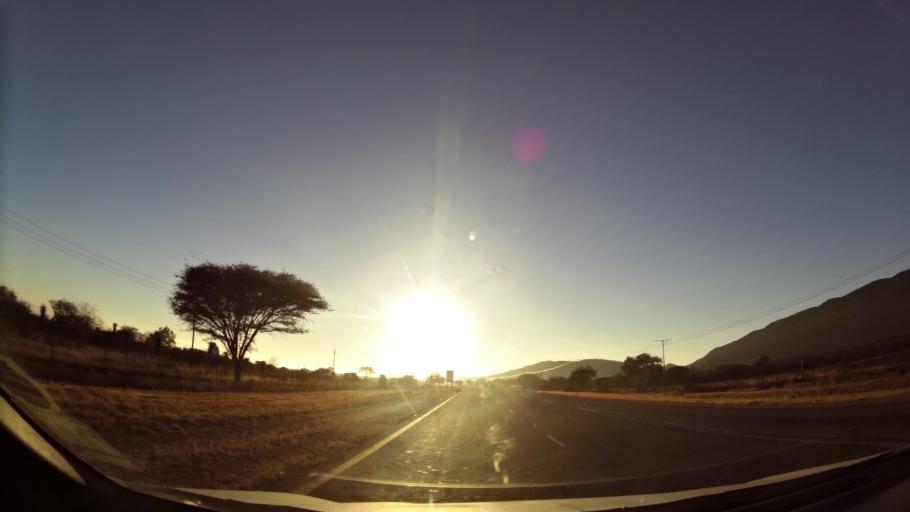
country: ZA
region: Limpopo
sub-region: Capricorn District Municipality
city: Polokwane
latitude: -24.0136
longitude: 29.3204
